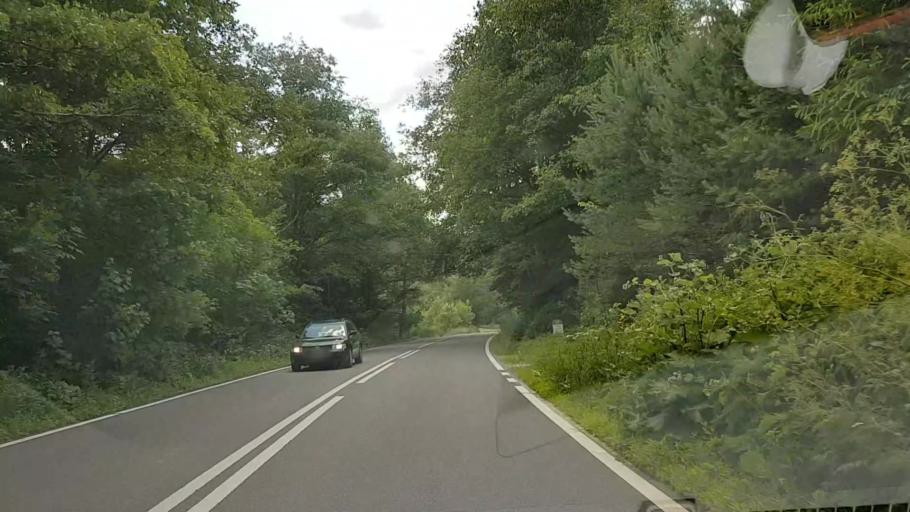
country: RO
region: Suceava
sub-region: Comuna Crucea
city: Crucea
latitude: 47.3277
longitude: 25.6209
